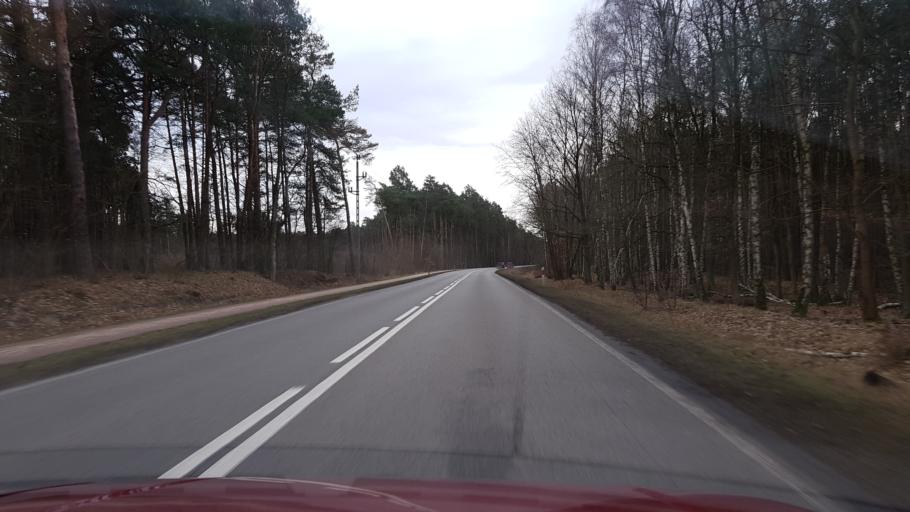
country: PL
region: West Pomeranian Voivodeship
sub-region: Powiat policki
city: Dobra
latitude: 53.5101
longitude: 14.4756
